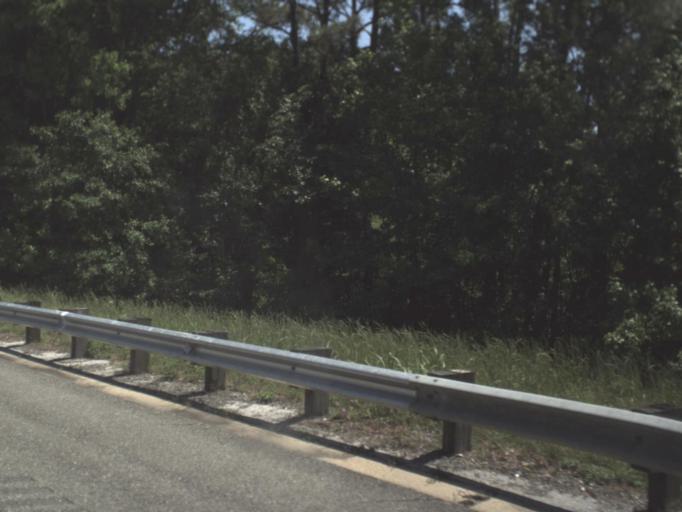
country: US
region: Florida
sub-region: Jefferson County
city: Monticello
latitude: 30.4739
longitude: -83.8818
